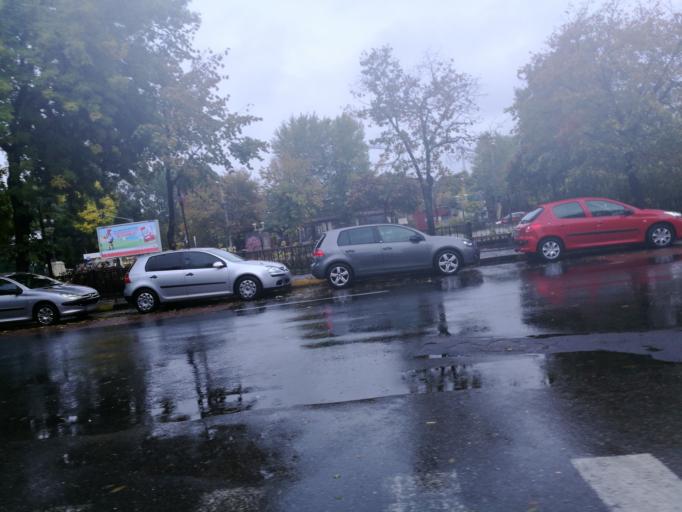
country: RO
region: Ilfov
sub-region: Comuna Chiajna
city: Rosu
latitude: 44.4449
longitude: 26.0531
